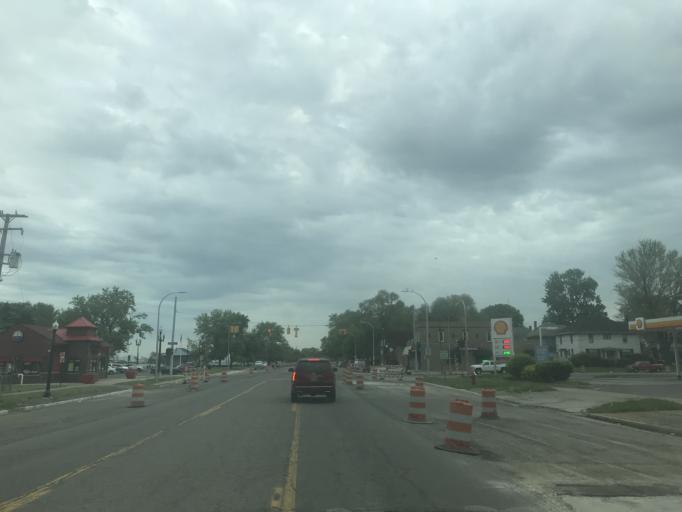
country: US
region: Michigan
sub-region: Wayne County
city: Ecorse
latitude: 42.2421
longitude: -83.1444
